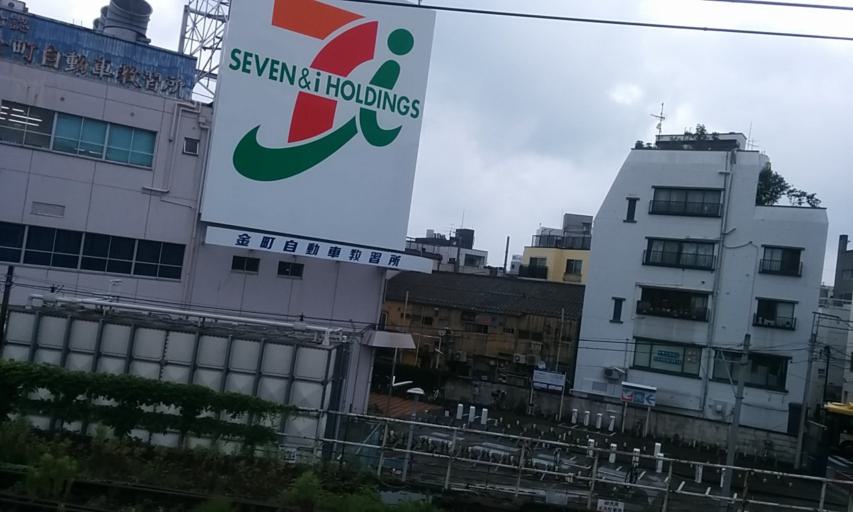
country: JP
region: Chiba
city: Matsudo
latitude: 35.7694
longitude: 139.8684
